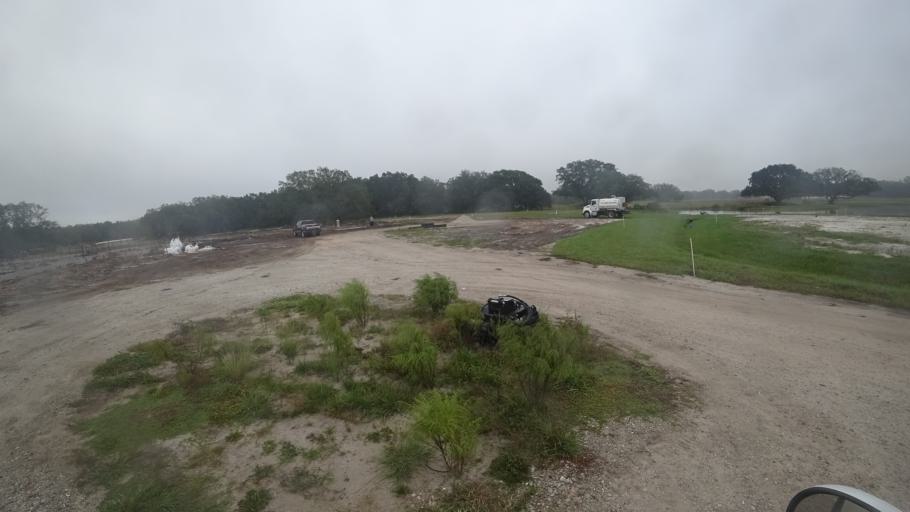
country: US
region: Florida
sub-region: Sarasota County
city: Lake Sarasota
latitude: 27.2926
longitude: -82.2193
